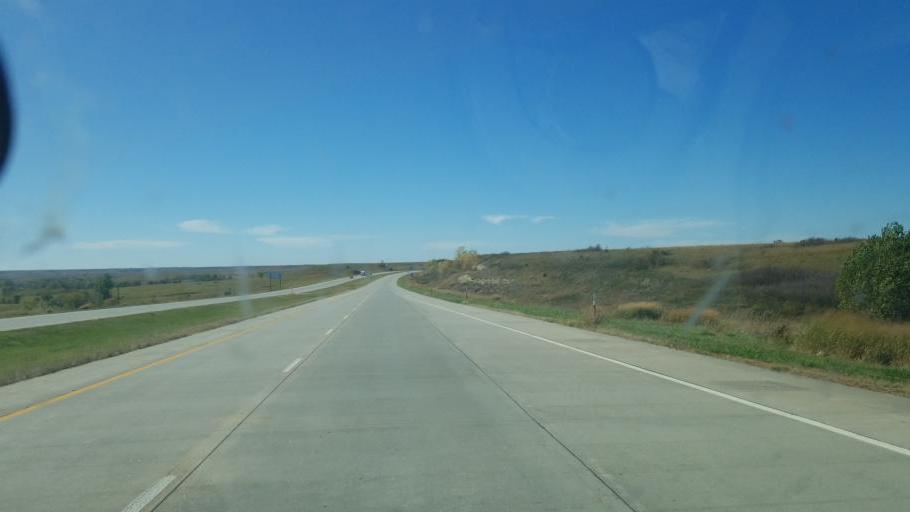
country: US
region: Kansas
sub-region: Riley County
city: Manhattan
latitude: 39.0629
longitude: -96.5426
